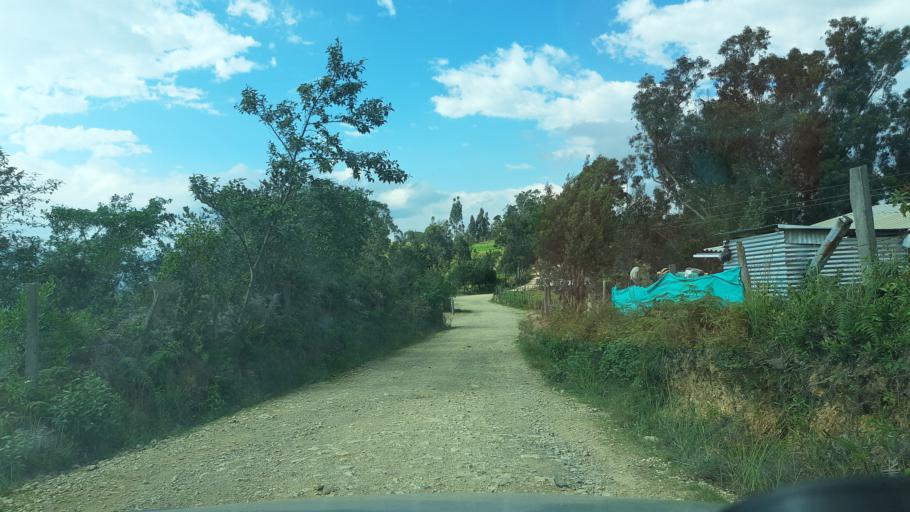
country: CO
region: Boyaca
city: Santa Sofia
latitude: 5.7387
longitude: -73.5519
